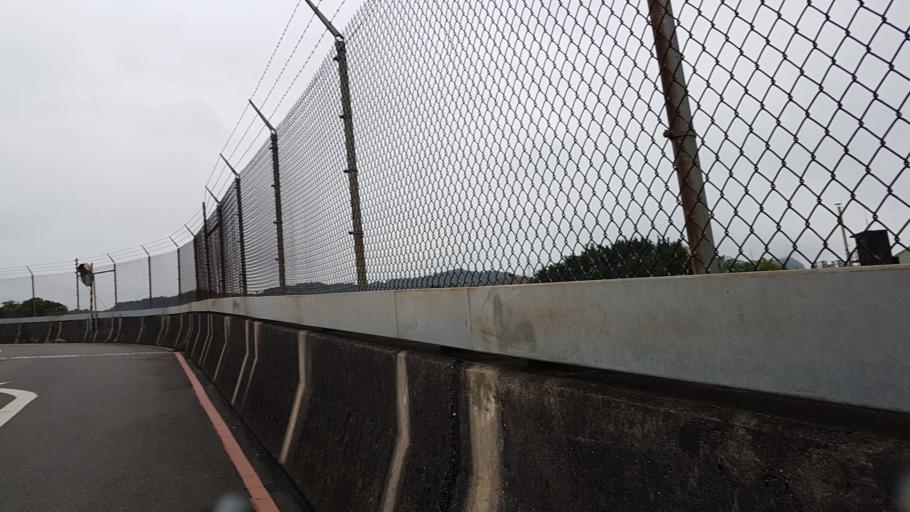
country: TW
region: Taipei
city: Taipei
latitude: 25.0498
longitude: 121.5958
